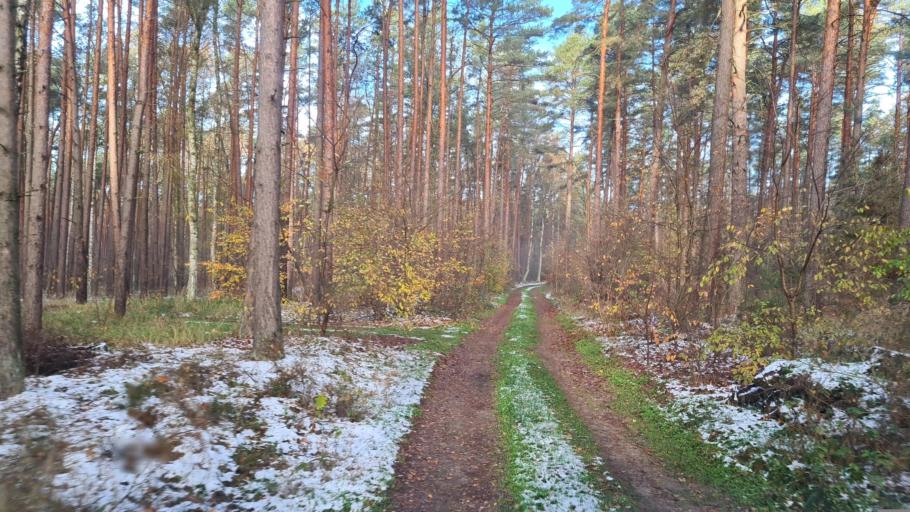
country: DE
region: Brandenburg
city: Bronkow
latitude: 51.6602
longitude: 13.8984
